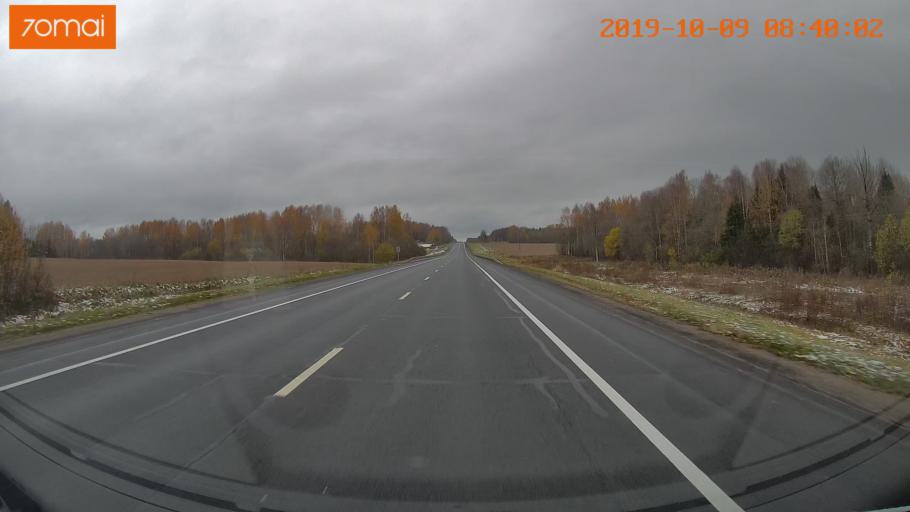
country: RU
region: Vologda
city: Gryazovets
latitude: 58.9804
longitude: 40.1456
